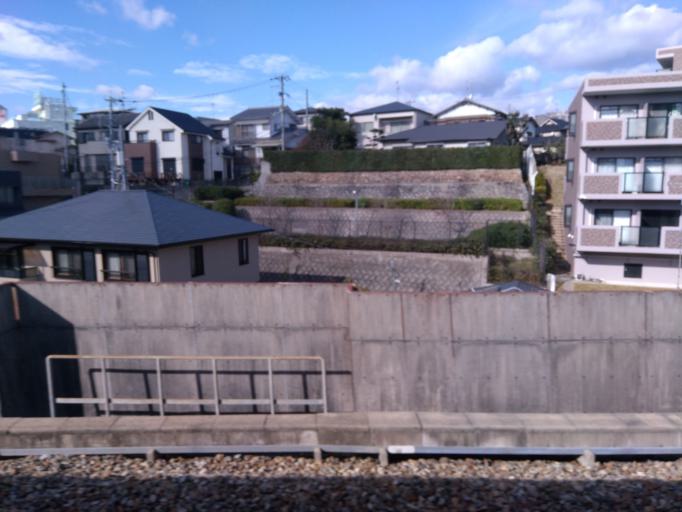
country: JP
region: Hyogo
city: Takarazuka
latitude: 34.8104
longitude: 135.3449
